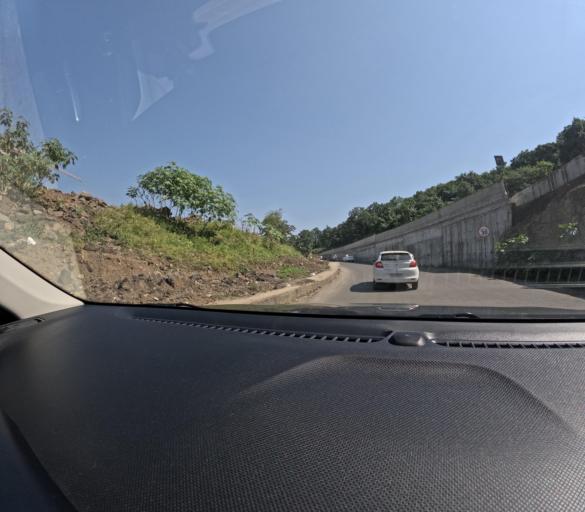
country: IN
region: Maharashtra
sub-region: Pune Division
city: Kharakvasla
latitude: 18.5053
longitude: 73.7856
